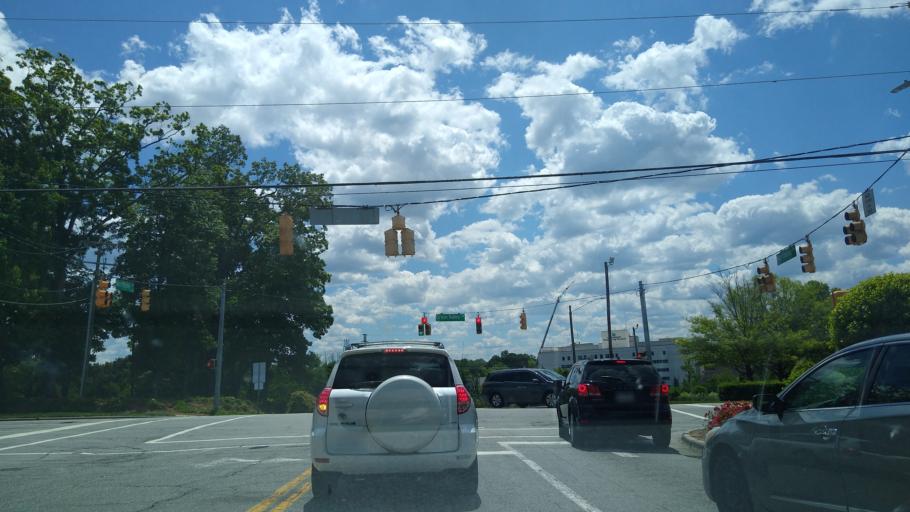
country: US
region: North Carolina
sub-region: Guilford County
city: Greensboro
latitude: 36.0864
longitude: -79.8279
